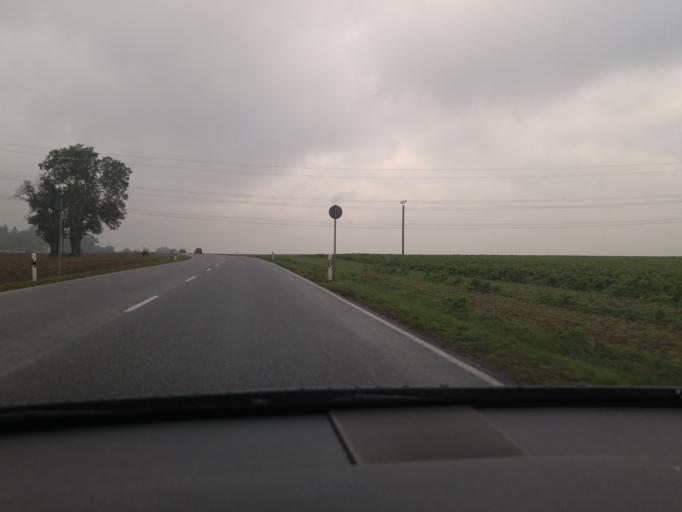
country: DE
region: Hesse
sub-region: Regierungsbezirk Darmstadt
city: Florstadt
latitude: 50.3250
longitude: 8.8191
